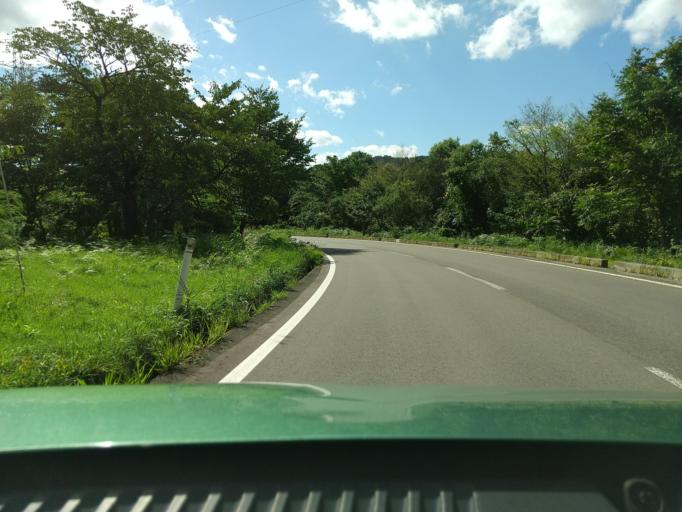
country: JP
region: Iwate
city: Shizukuishi
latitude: 39.7657
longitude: 140.7499
